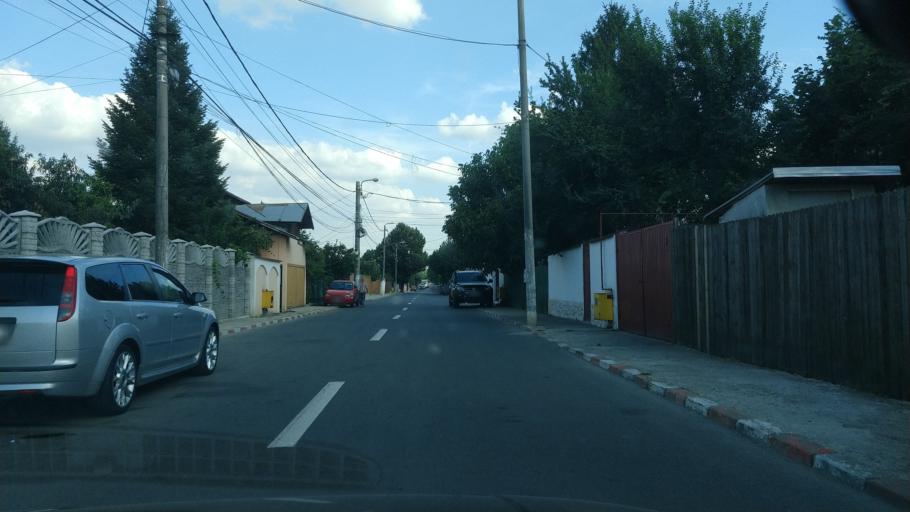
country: RO
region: Ilfov
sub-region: Voluntari City
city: Voluntari
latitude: 44.4913
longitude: 26.1655
